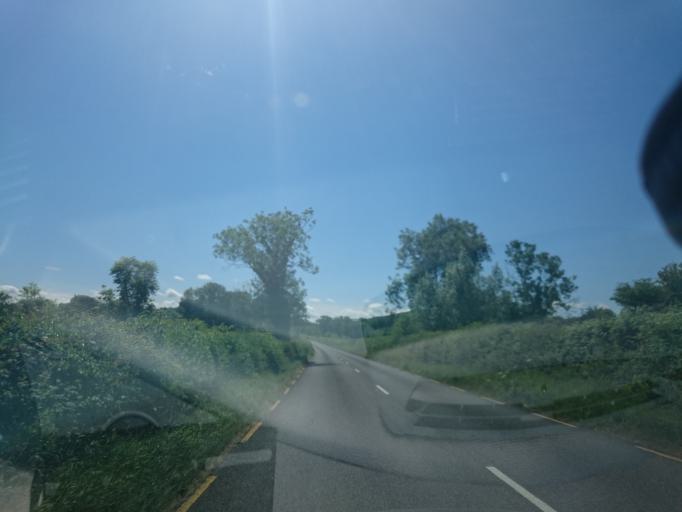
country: IE
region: Leinster
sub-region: Kilkenny
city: Graiguenamanagh
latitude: 52.5703
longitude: -6.9530
